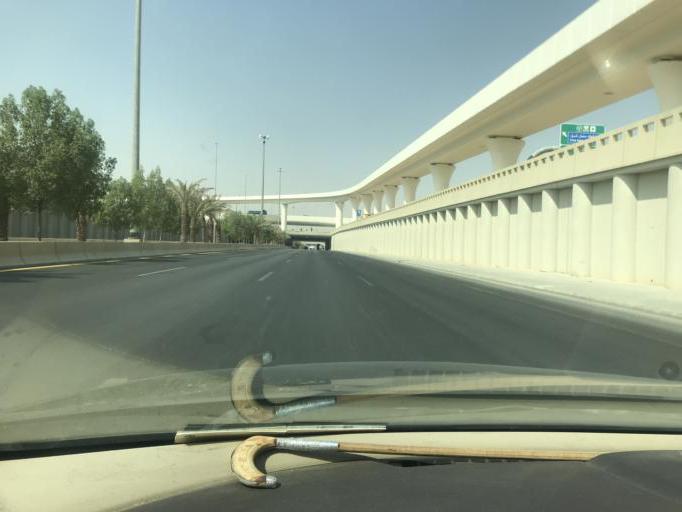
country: SA
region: Ar Riyad
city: Riyadh
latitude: 24.8445
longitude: 46.6563
